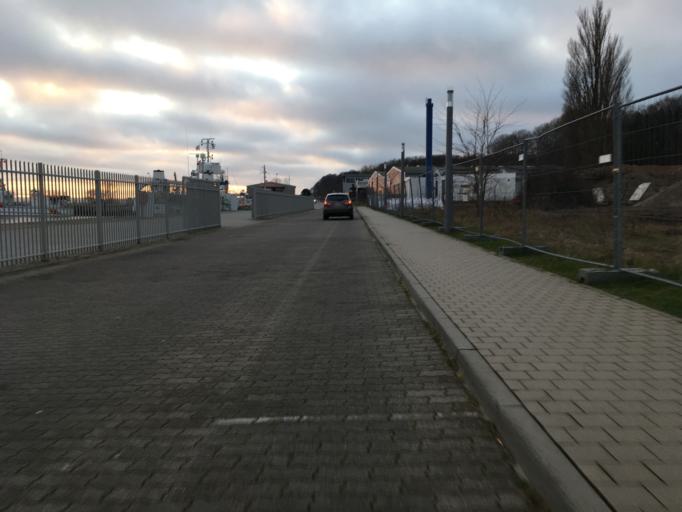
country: DE
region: Mecklenburg-Vorpommern
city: Sassnitz
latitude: 54.5103
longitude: 13.6359
